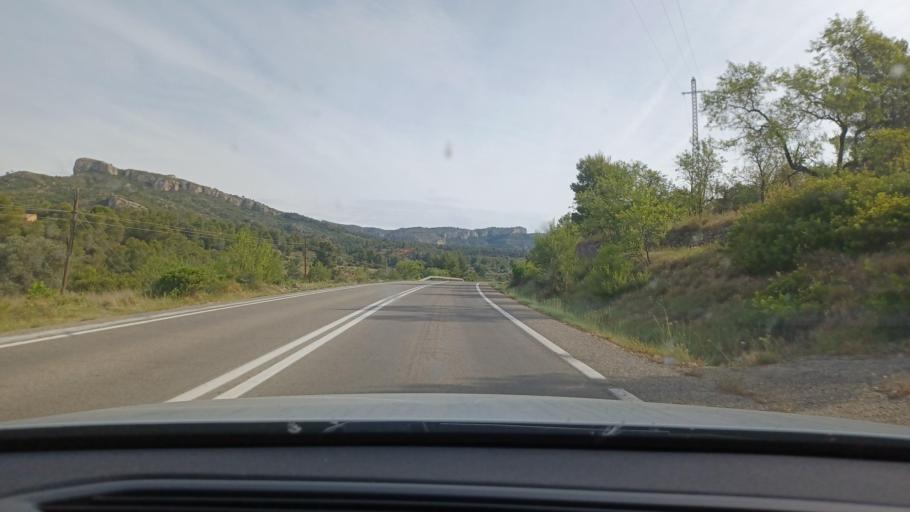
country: ES
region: Catalonia
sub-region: Provincia de Tarragona
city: Benifallet
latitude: 41.0247
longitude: 0.4984
